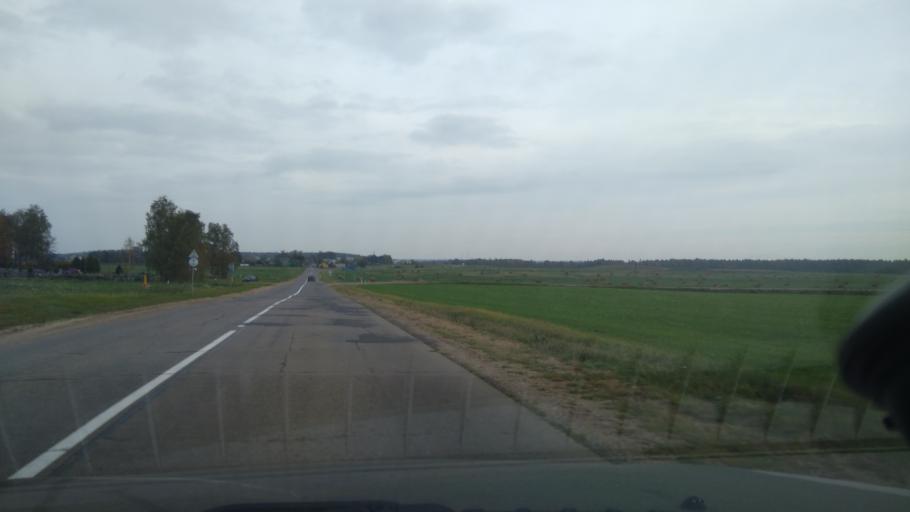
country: BY
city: Michanovichi
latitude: 53.6137
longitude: 27.7054
